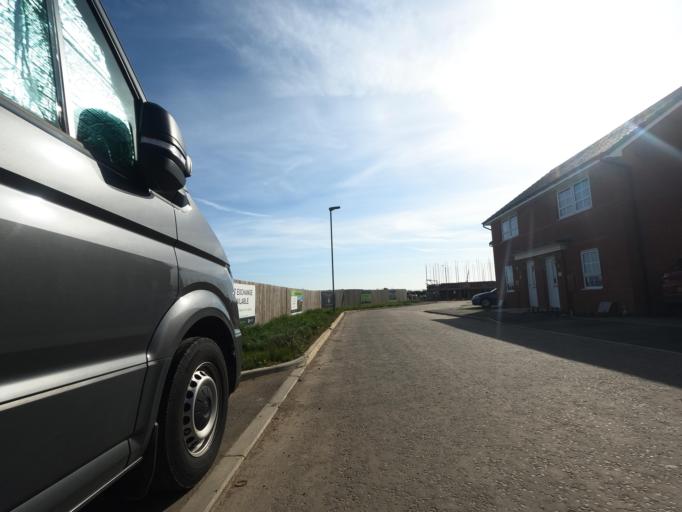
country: GB
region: England
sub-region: Northumberland
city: Morpeth
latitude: 55.1568
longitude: -1.6692
